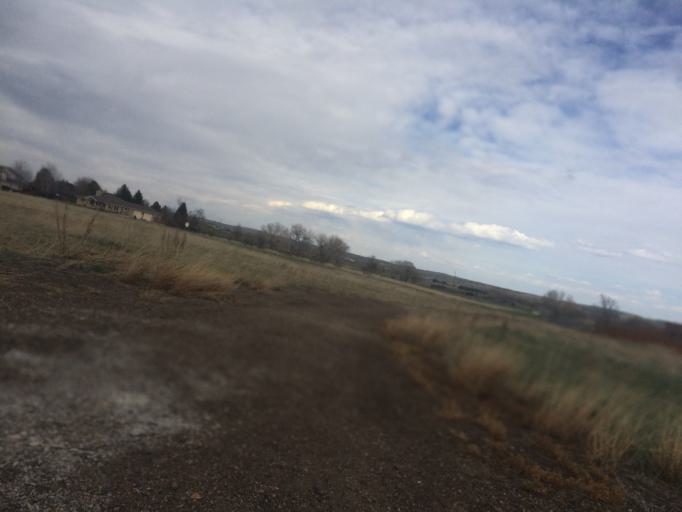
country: US
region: Colorado
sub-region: Boulder County
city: Superior
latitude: 39.9526
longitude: -105.1499
